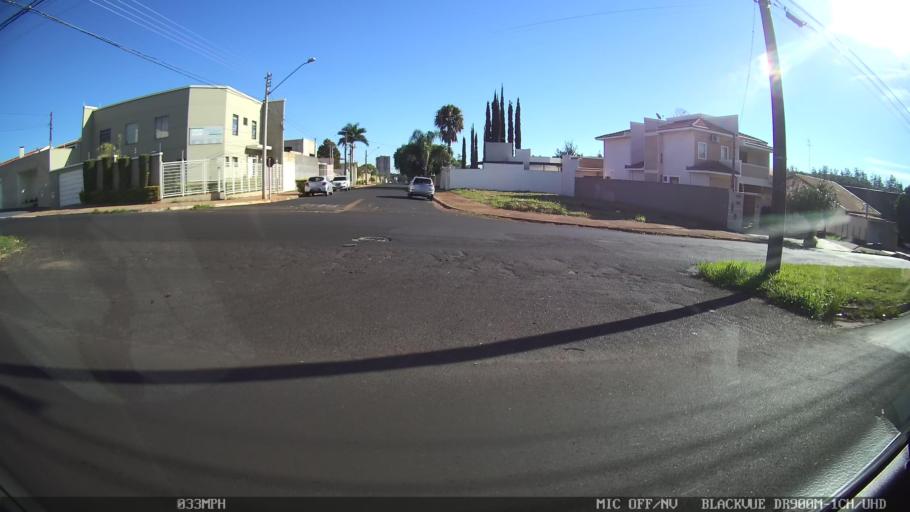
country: BR
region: Sao Paulo
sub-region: Araraquara
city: Araraquara
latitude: -21.7603
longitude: -48.1764
